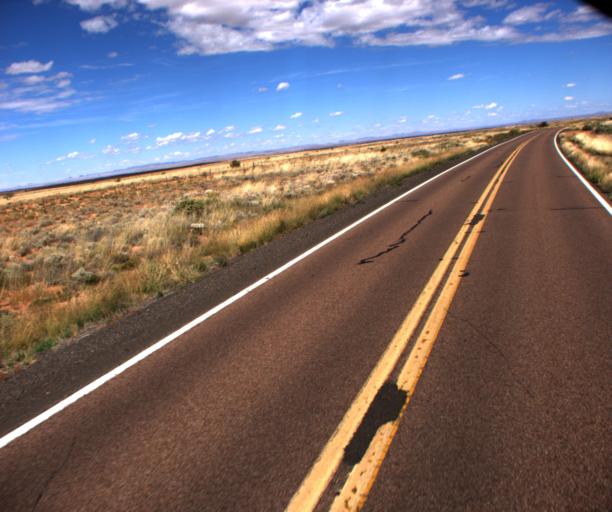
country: US
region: Arizona
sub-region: Navajo County
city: Holbrook
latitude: 34.7210
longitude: -110.2939
